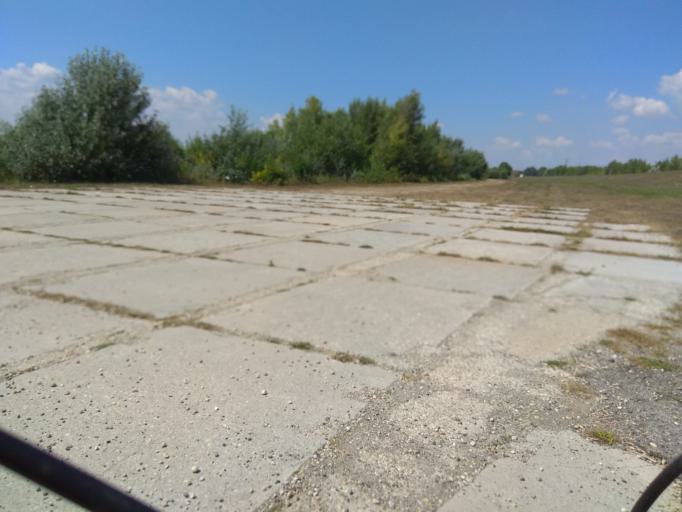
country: SK
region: Trnavsky
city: Gabcikovo
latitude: 47.8749
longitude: 17.5524
